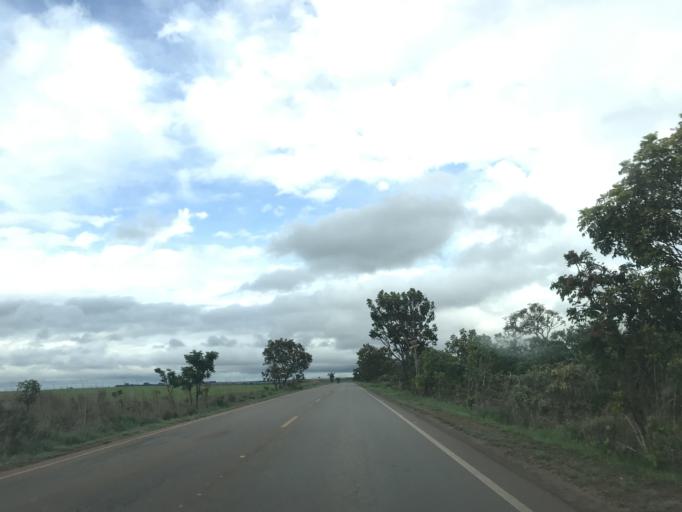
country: BR
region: Goias
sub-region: Vianopolis
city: Vianopolis
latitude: -16.5713
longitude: -48.2930
